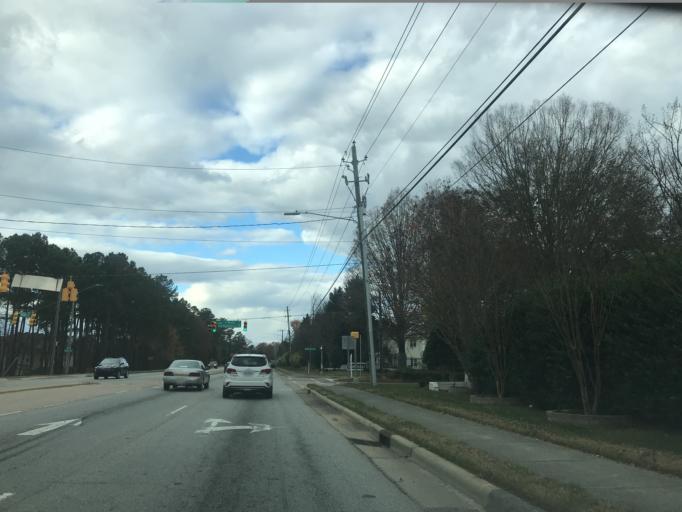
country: US
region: North Carolina
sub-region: Wake County
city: Raleigh
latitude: 35.8159
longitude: -78.5672
